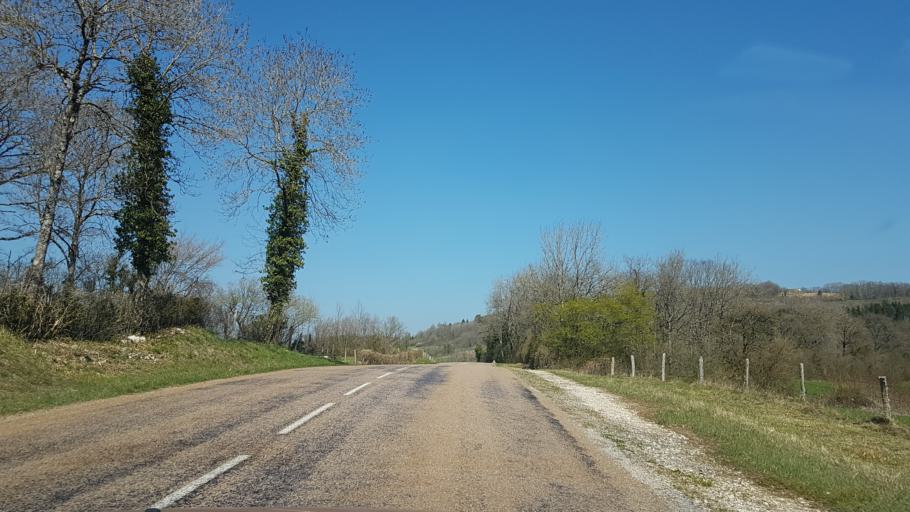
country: FR
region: Franche-Comte
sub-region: Departement du Jura
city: Orgelet
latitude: 46.5417
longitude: 5.6510
